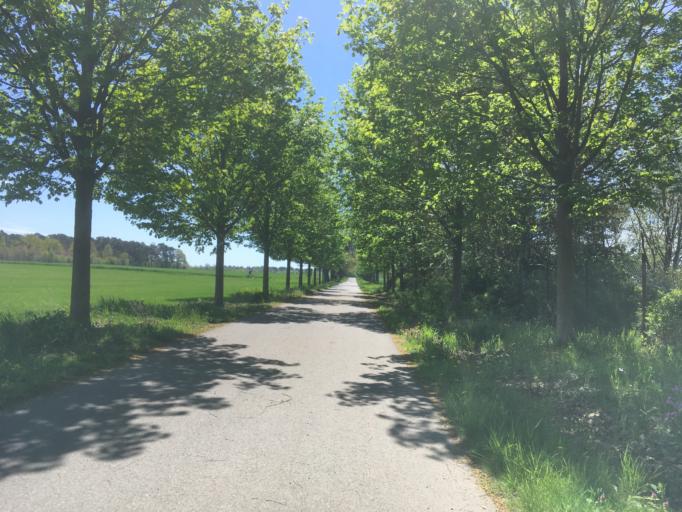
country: DE
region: Brandenburg
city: Wildau
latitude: 52.3185
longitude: 13.6135
